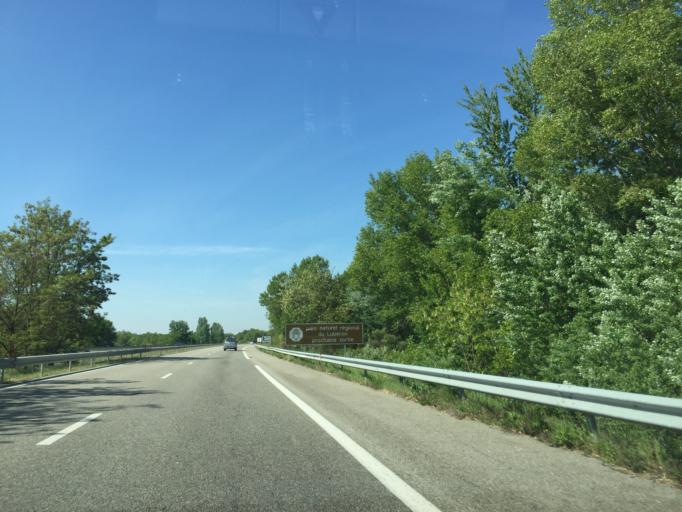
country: FR
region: Provence-Alpes-Cote d'Azur
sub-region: Departement des Alpes-de-Haute-Provence
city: Volx
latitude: 43.8246
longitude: 5.8362
